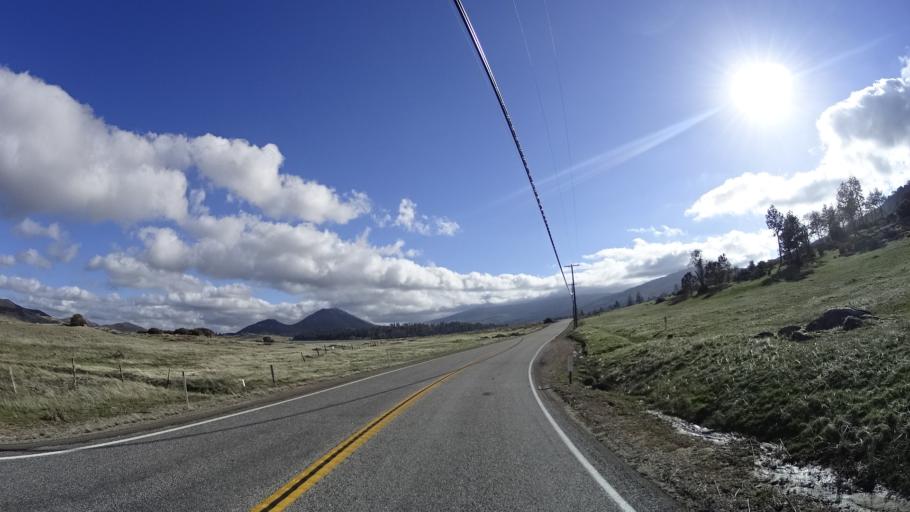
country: US
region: California
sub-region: San Diego County
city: Julian
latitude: 32.9993
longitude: -116.5662
